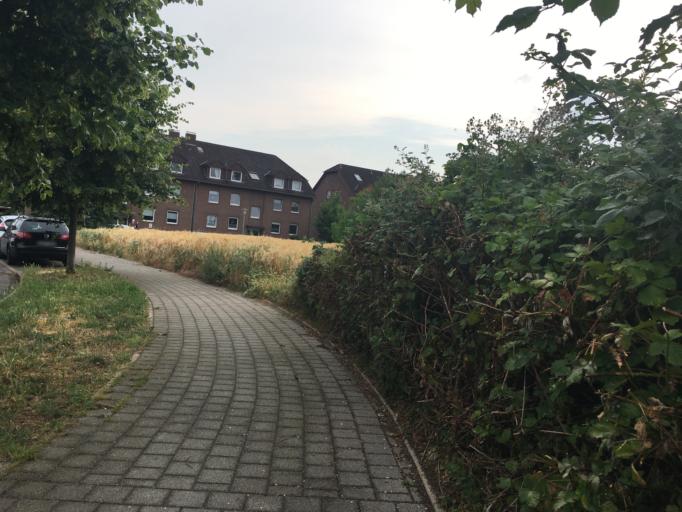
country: DE
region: North Rhine-Westphalia
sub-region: Regierungsbezirk Dusseldorf
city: Dinslaken
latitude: 51.5401
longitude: 6.7122
